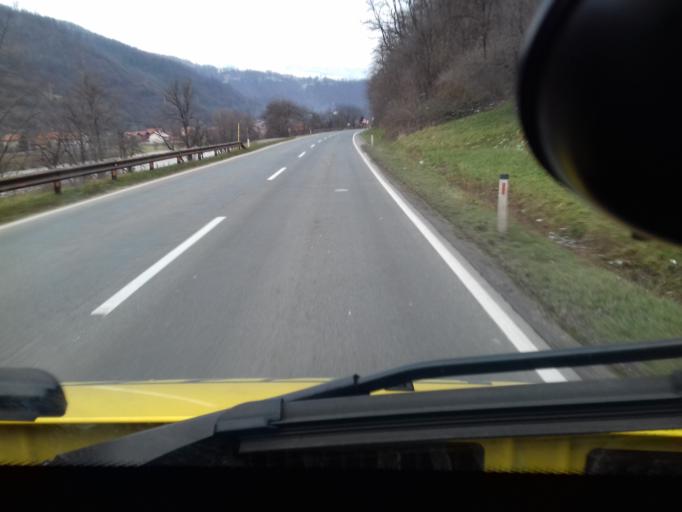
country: BA
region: Federation of Bosnia and Herzegovina
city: Zeljezno Polje
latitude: 44.3151
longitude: 17.9038
